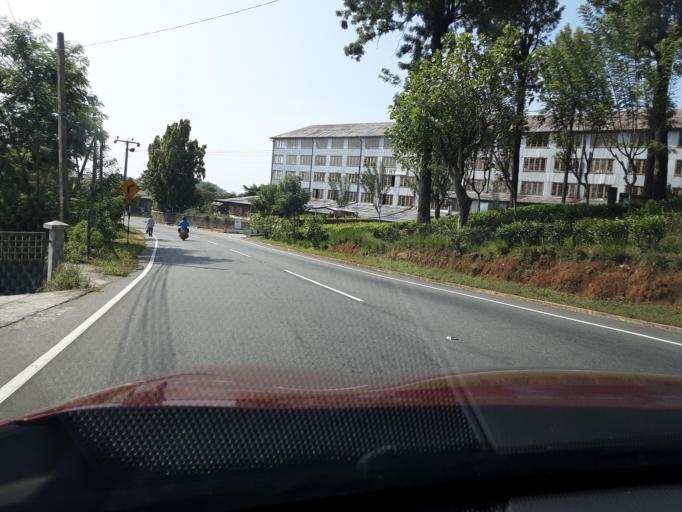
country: LK
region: Uva
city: Badulla
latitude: 6.9513
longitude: 81.1243
